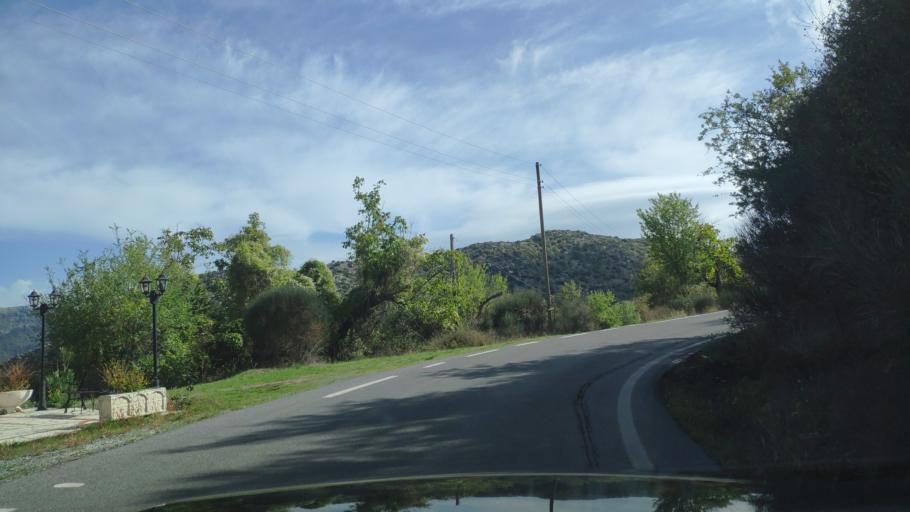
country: GR
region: Peloponnese
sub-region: Nomos Arkadias
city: Dimitsana
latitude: 37.5873
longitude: 22.0199
